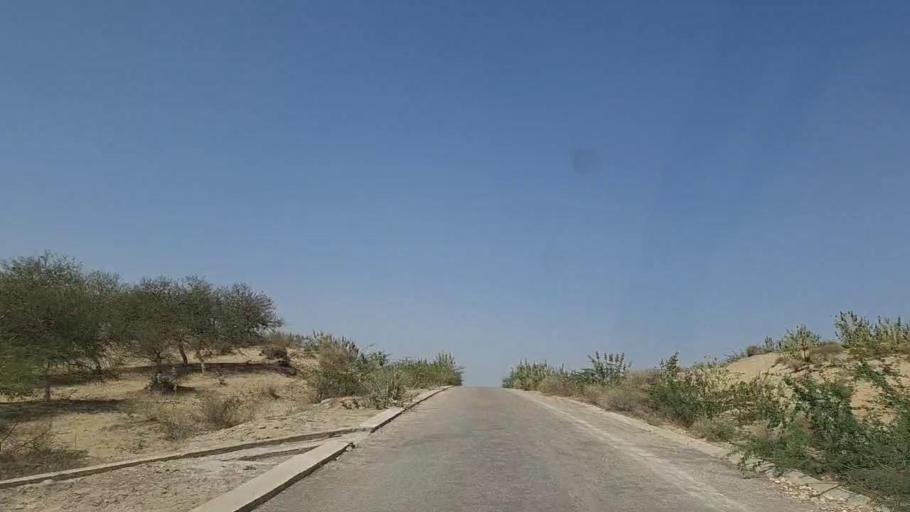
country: PK
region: Sindh
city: Diplo
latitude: 24.5820
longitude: 69.3197
